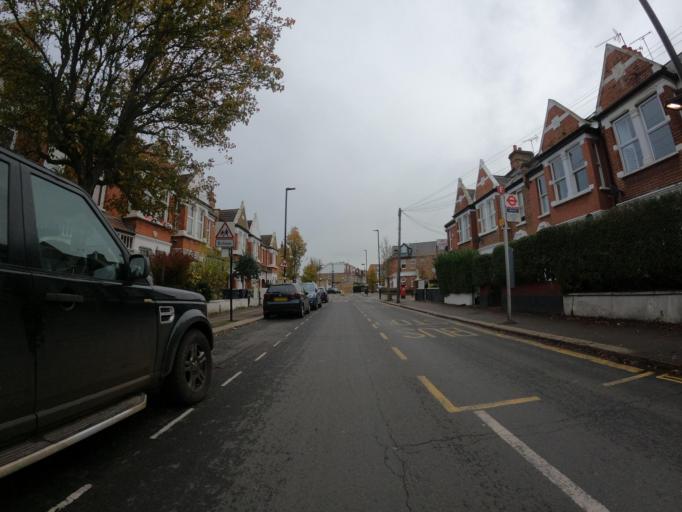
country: GB
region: England
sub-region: Greater London
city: Acton
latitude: 51.5018
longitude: -0.2575
